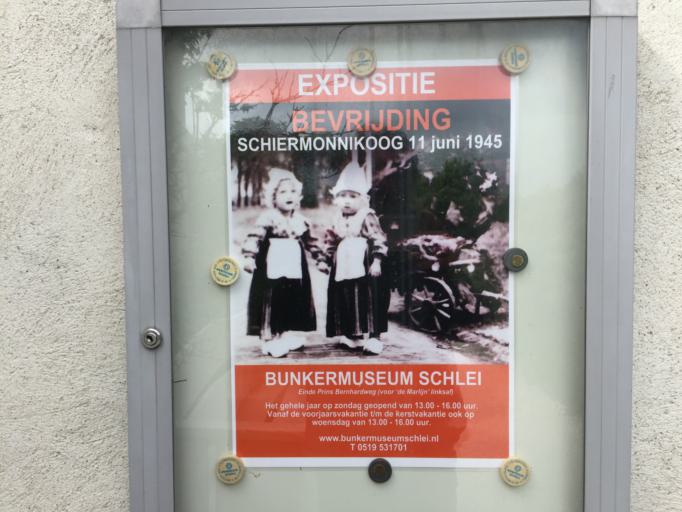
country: NL
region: Friesland
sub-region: Gemeente Schiermonnikoog
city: Schiermonnikoog
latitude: 53.4969
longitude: 6.1859
